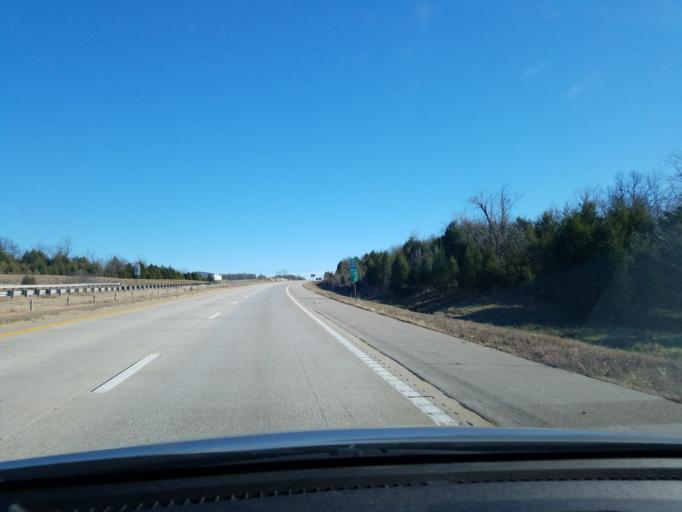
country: US
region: Missouri
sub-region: Pulaski County
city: Richland
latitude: 37.7602
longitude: -92.5178
